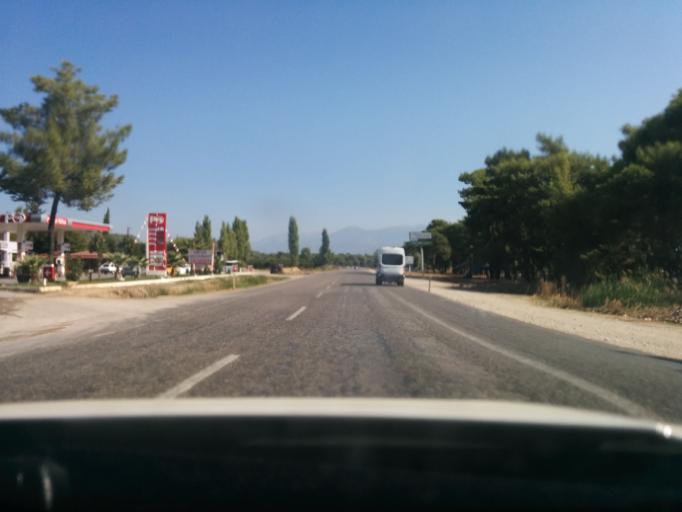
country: TR
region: Mugla
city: Esen
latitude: 36.4737
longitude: 29.2999
